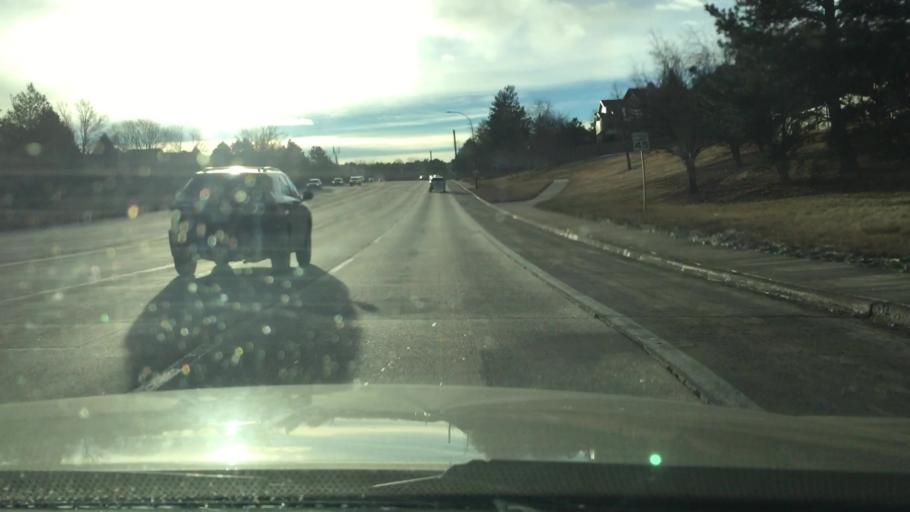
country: US
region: Colorado
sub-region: Douglas County
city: Highlands Ranch
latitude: 39.5437
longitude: -104.9711
